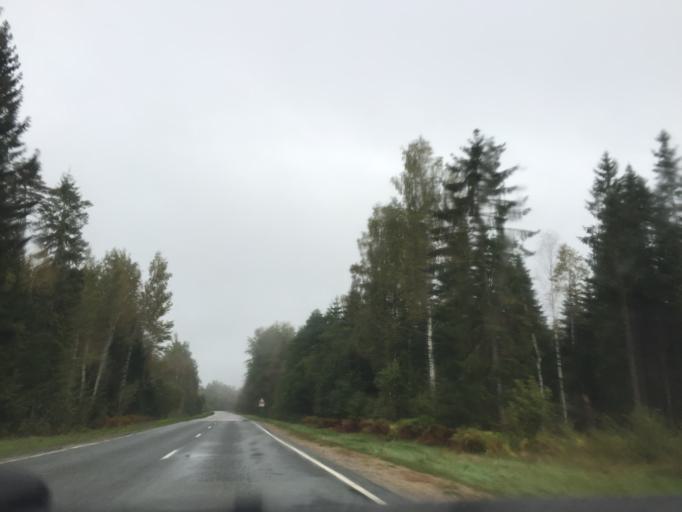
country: LV
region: Incukalns
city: Incukalns
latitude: 57.0509
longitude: 24.6750
